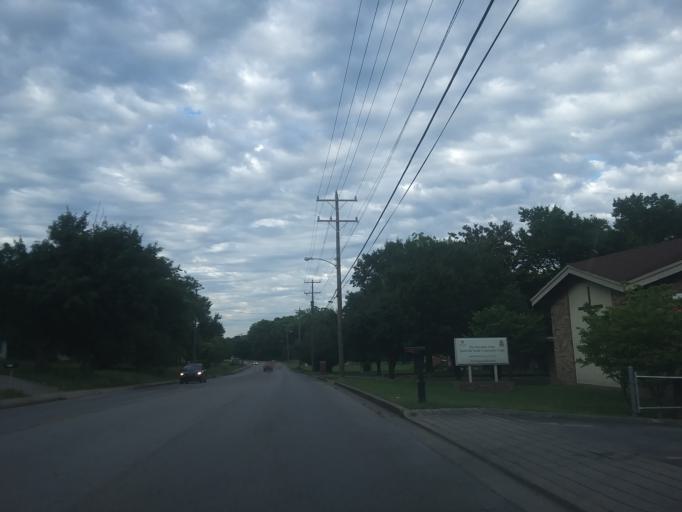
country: US
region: Tennessee
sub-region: Davidson County
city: Oak Hill
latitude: 36.0861
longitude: -86.7259
